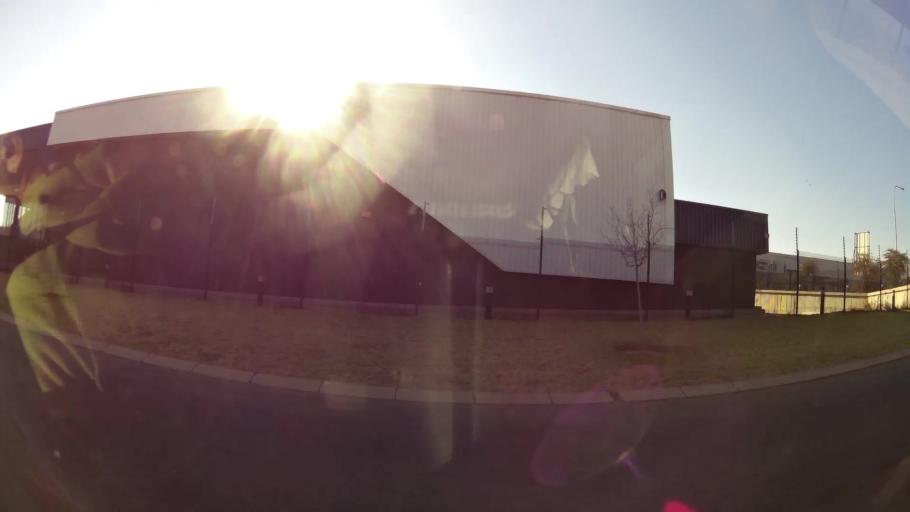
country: ZA
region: Gauteng
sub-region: City of Johannesburg Metropolitan Municipality
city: Modderfontein
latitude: -26.0540
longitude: 28.1686
